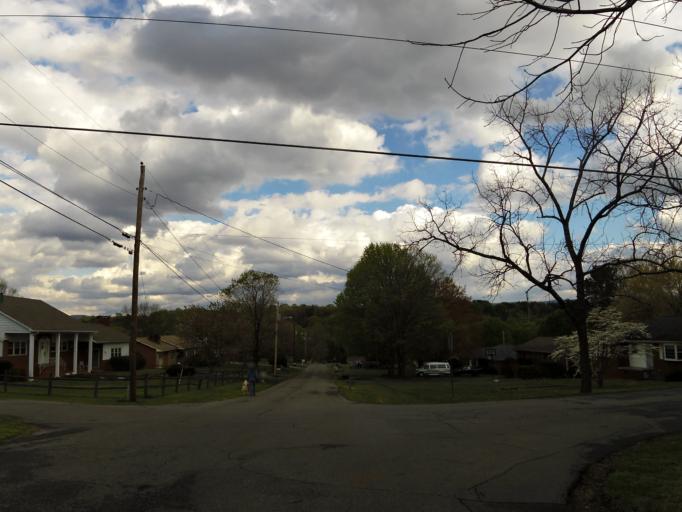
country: US
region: Tennessee
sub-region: Blount County
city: Maryville
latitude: 35.7400
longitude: -83.9796
